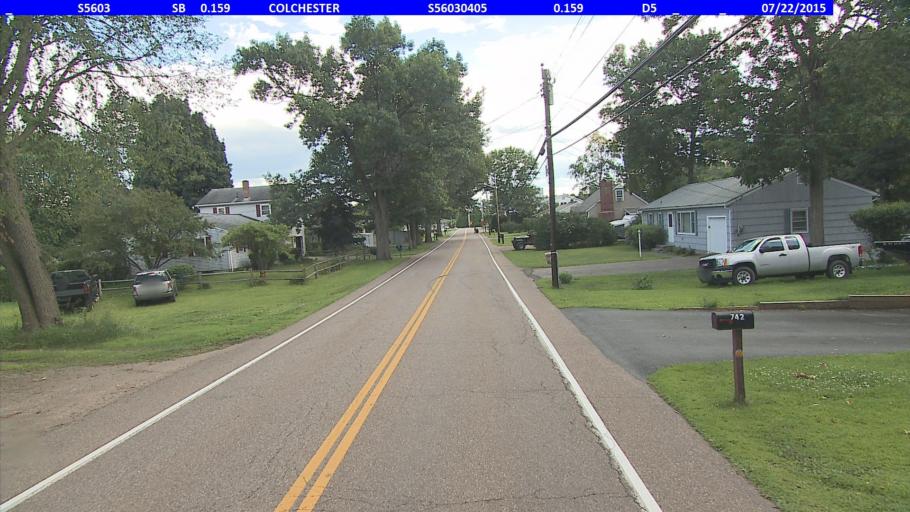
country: US
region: Vermont
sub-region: Chittenden County
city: Burlington
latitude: 44.5403
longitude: -73.2504
